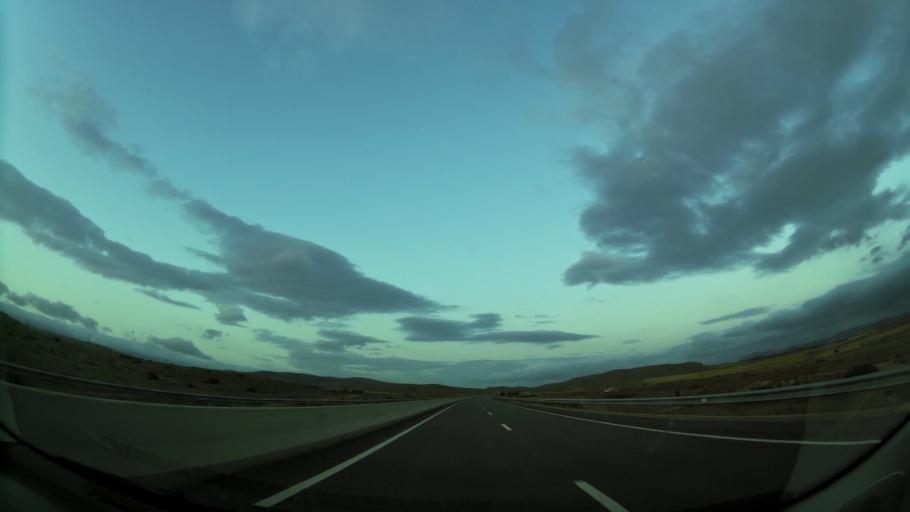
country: MA
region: Oriental
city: El Aioun
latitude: 34.6044
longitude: -2.6196
